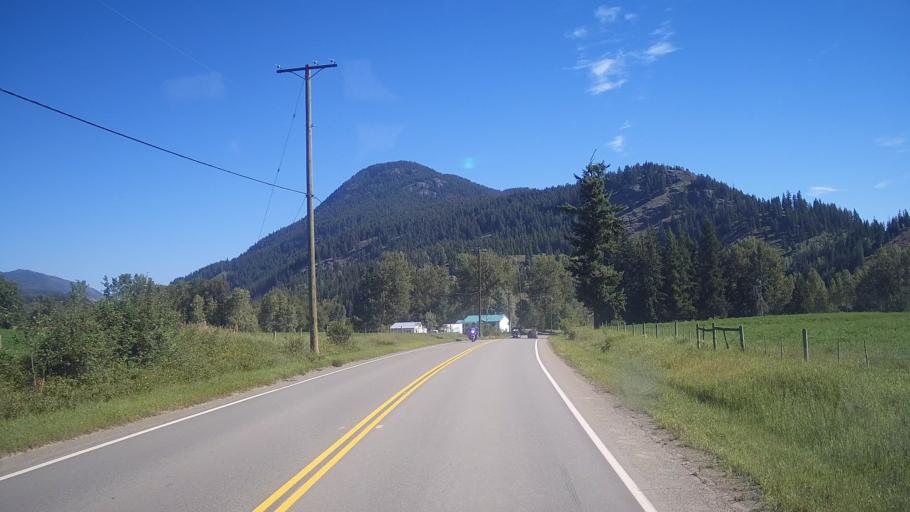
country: CA
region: British Columbia
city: Kamloops
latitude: 51.4293
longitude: -120.2105
